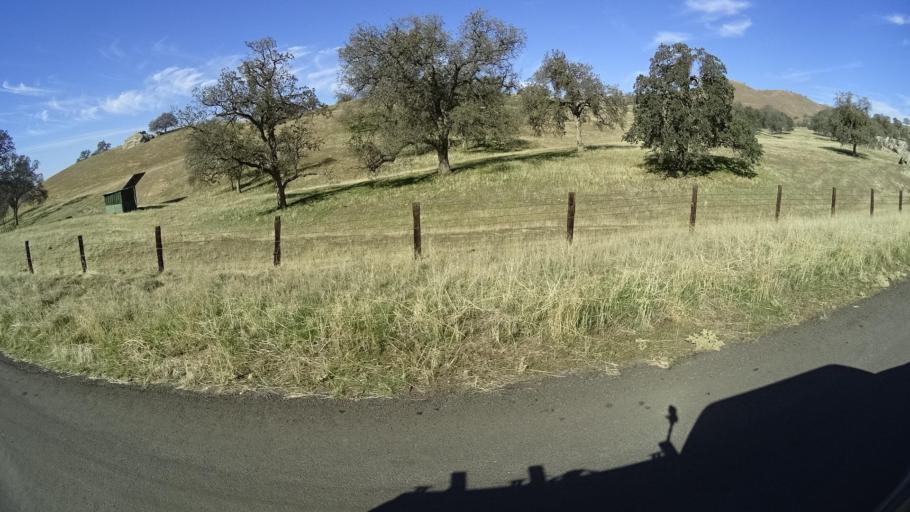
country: US
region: California
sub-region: Tulare County
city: Richgrove
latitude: 35.6754
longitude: -118.8505
